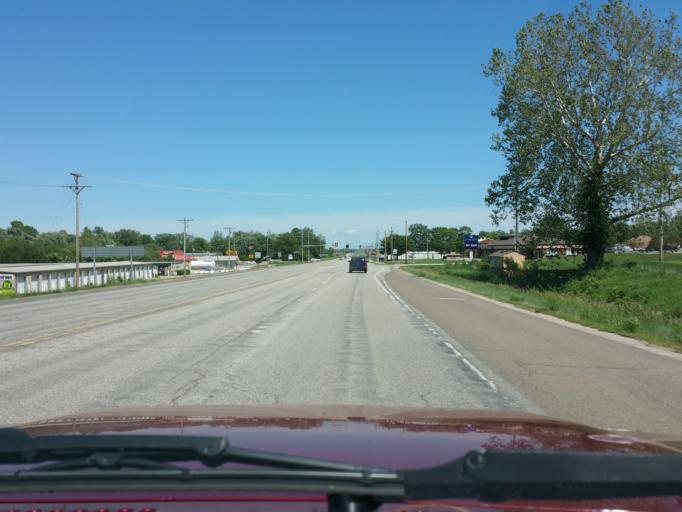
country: US
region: Kansas
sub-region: Pottawatomie County
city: Wamego
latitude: 39.2102
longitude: -96.3183
